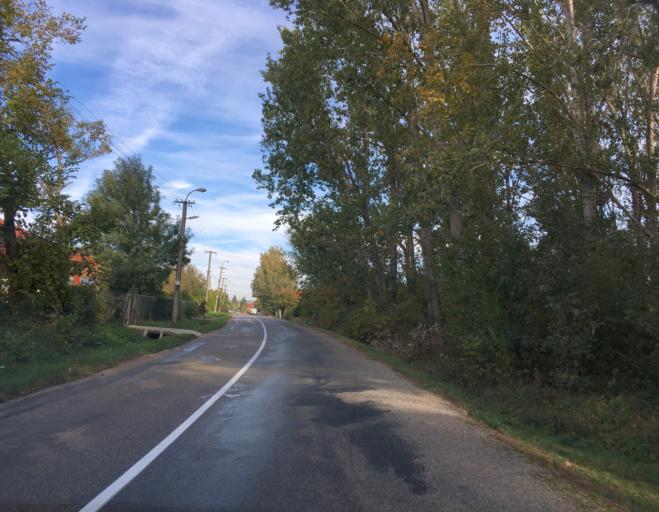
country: SK
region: Nitriansky
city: Svodin
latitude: 48.0061
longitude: 18.4145
